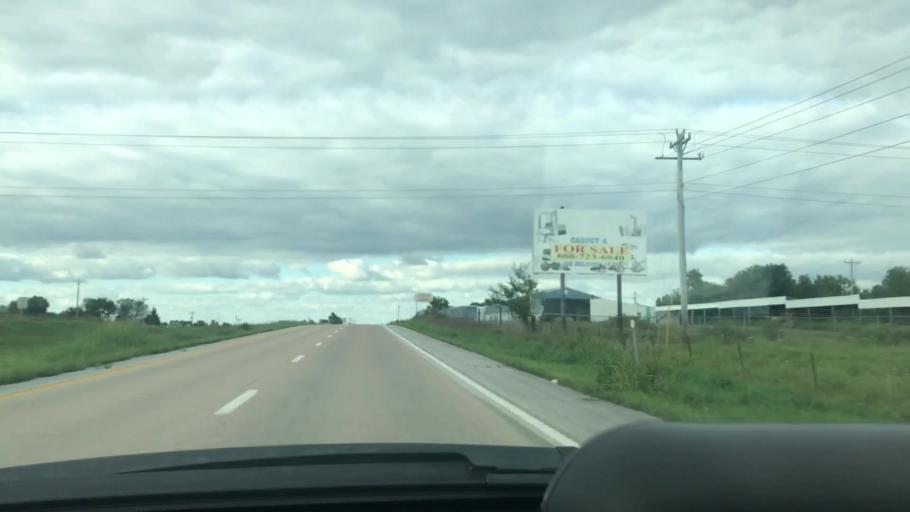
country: US
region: Missouri
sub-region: Benton County
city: Lincoln
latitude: 38.3304
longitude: -93.3414
